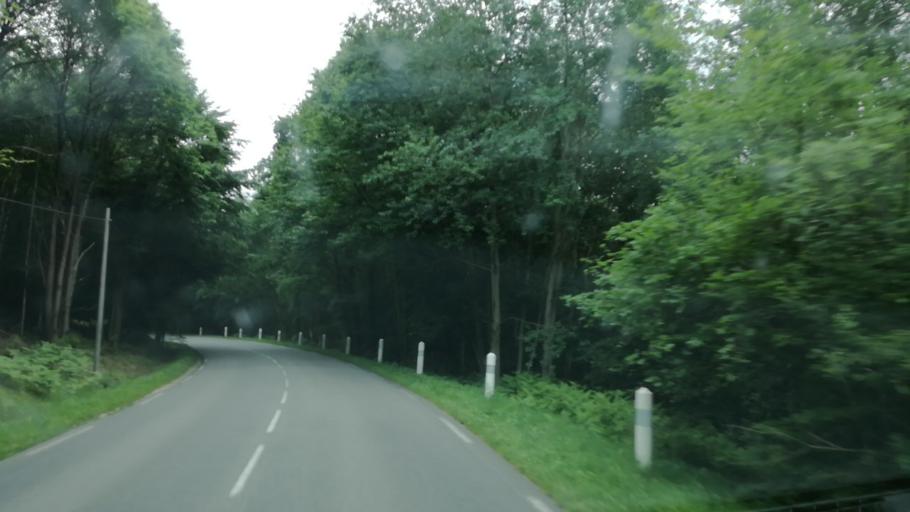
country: FR
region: Haute-Normandie
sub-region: Departement de l'Eure
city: Bourgtheroulde-Infreville
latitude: 49.2647
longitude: 0.8135
